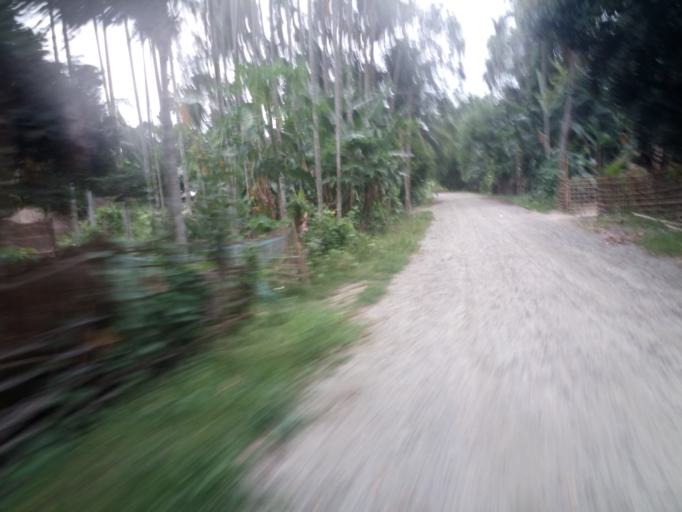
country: IN
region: Assam
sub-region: Darrang
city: Kharupatia
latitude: 26.6511
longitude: 92.2421
